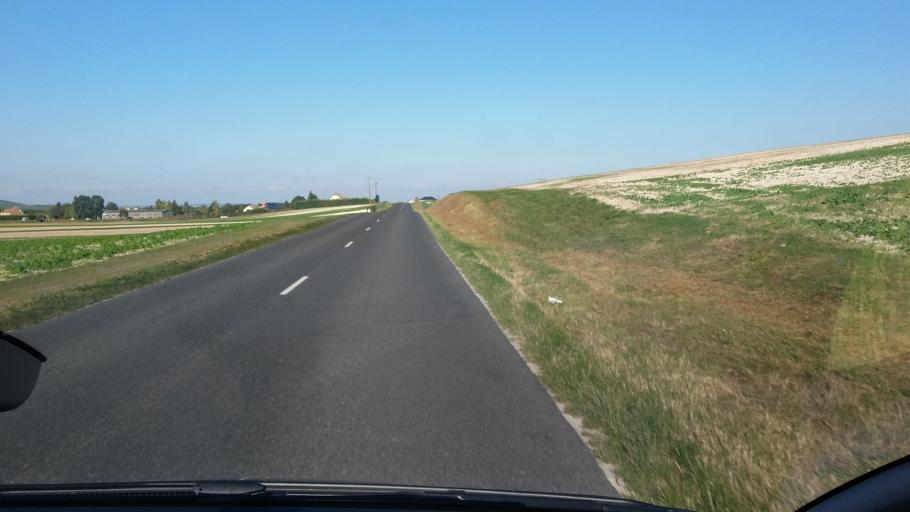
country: FR
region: Champagne-Ardenne
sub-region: Departement de la Marne
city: Vertus
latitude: 48.8690
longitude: 3.9914
